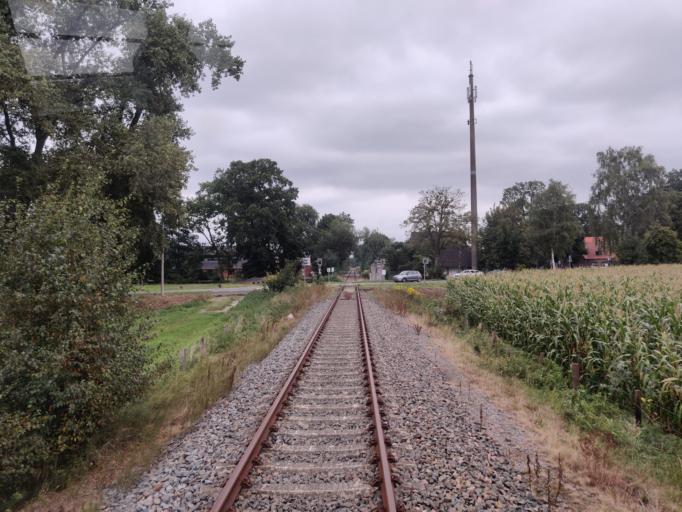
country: DE
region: Lower Saxony
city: Vollersode
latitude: 53.3128
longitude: 8.9747
